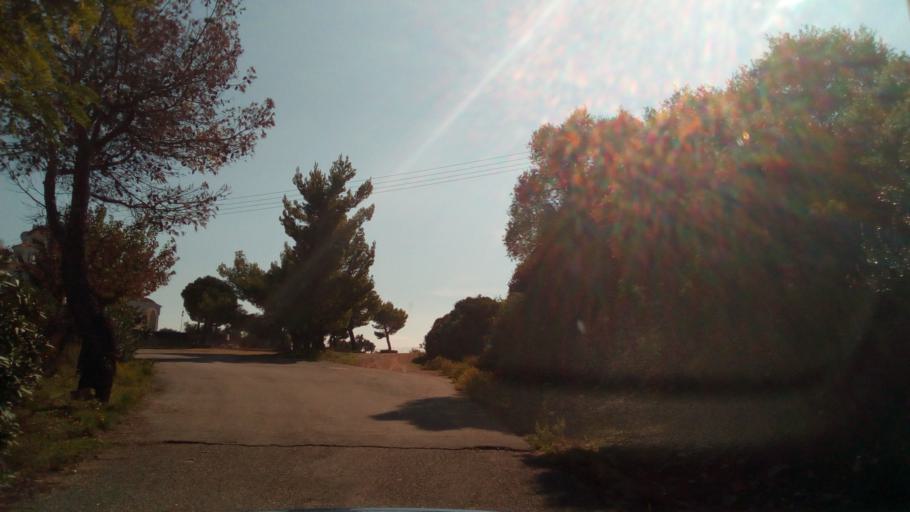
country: GR
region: West Greece
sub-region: Nomos Aitolias kai Akarnanias
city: Nafpaktos
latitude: 38.4173
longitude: 21.8501
